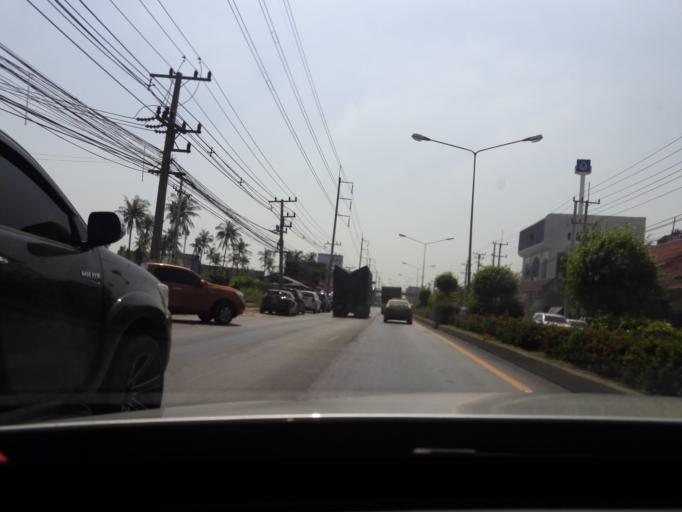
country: TH
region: Samut Sakhon
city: Samut Sakhon
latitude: 13.5872
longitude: 100.2794
